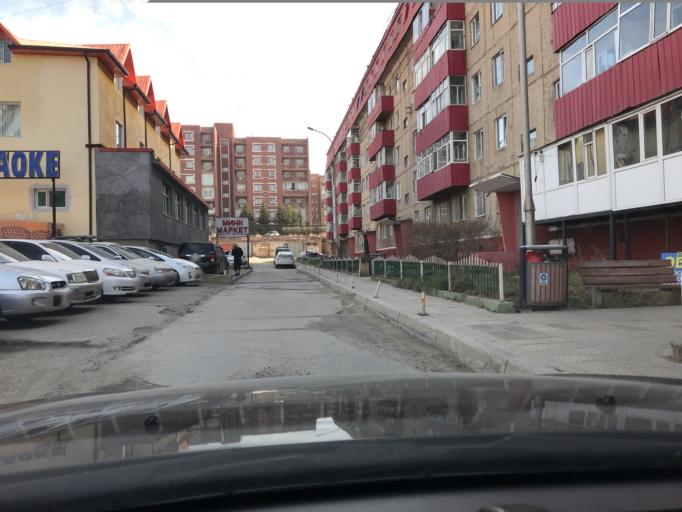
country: MN
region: Ulaanbaatar
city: Ulaanbaatar
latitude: 47.9213
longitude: 106.9441
